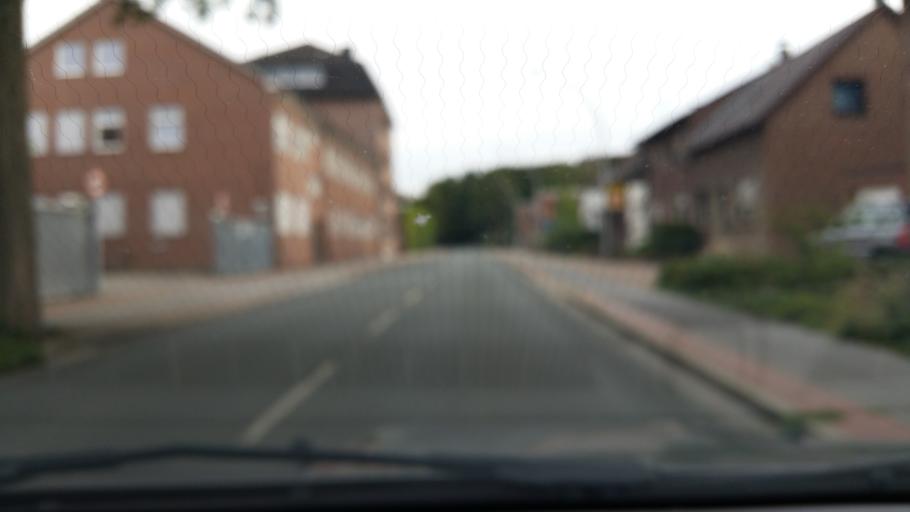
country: DE
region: North Rhine-Westphalia
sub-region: Regierungsbezirk Dusseldorf
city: Bocholt
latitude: 51.8467
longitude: 6.6198
